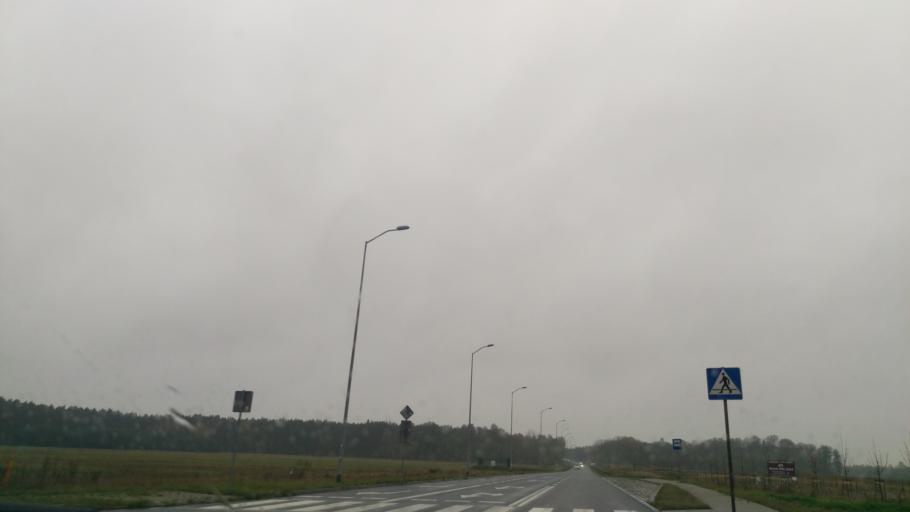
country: PL
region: West Pomeranian Voivodeship
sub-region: Powiat gryfinski
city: Stare Czarnowo
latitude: 53.4005
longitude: 14.7083
